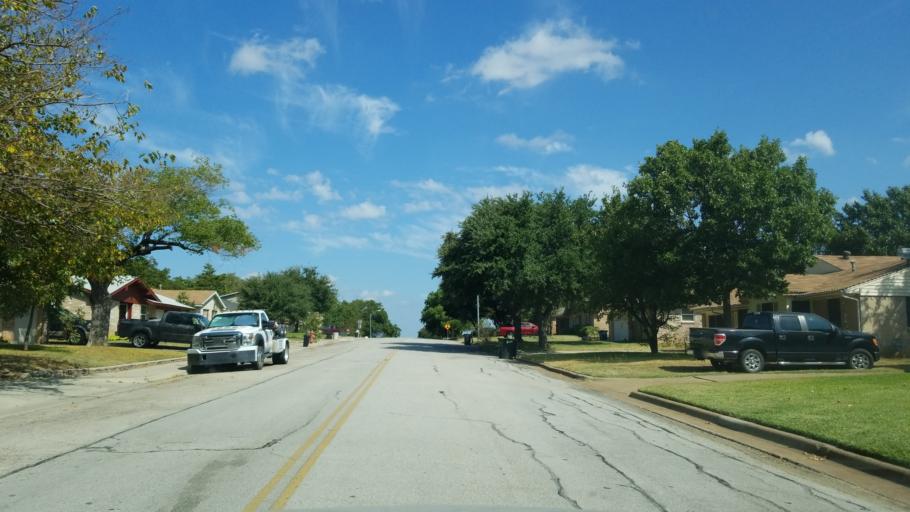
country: US
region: Texas
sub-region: Tarrant County
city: Euless
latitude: 32.8549
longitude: -97.0903
